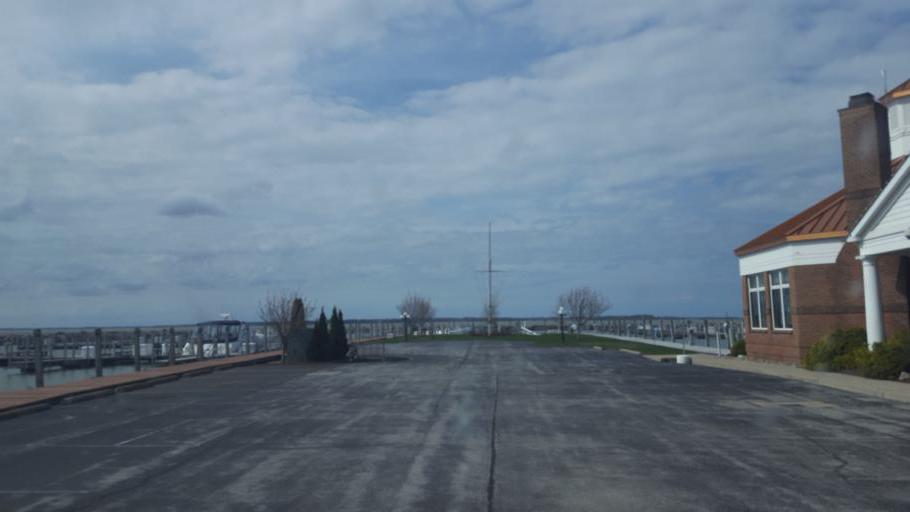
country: US
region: Ohio
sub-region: Erie County
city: Sandusky
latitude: 41.4608
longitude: -82.7061
